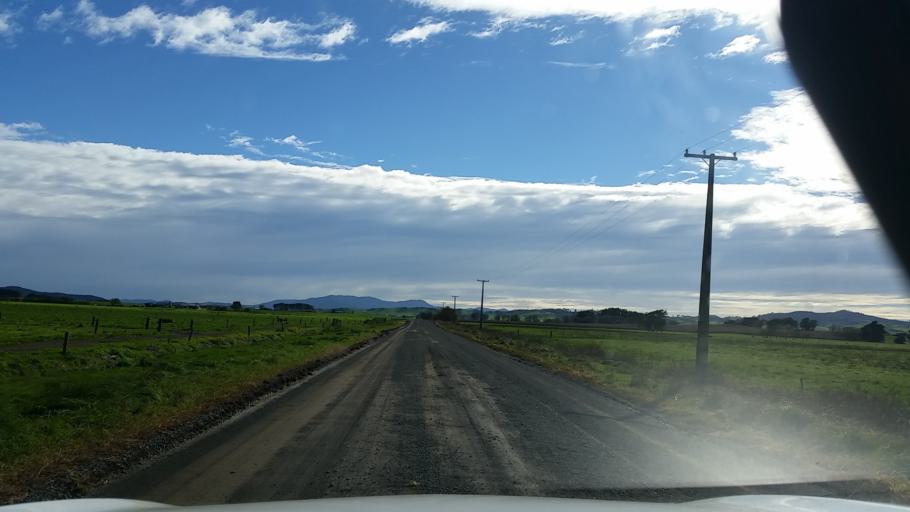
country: NZ
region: Waikato
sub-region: Hamilton City
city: Hamilton
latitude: -37.6393
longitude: 175.4308
